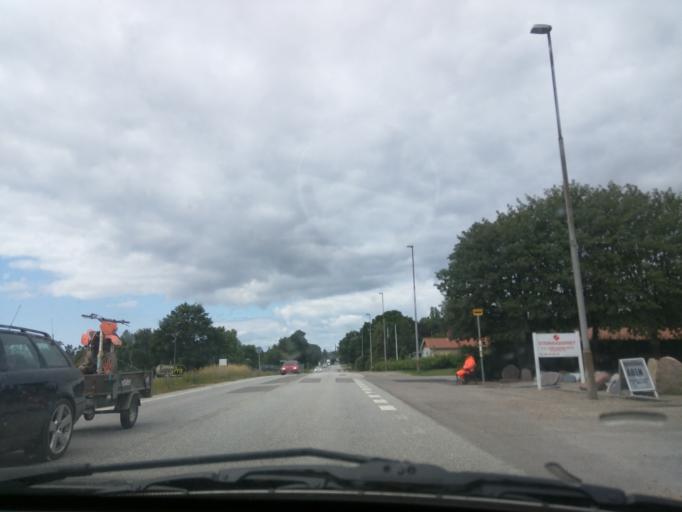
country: DK
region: Zealand
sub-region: Kalundborg Kommune
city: Kalundborg
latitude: 55.6807
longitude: 11.1238
